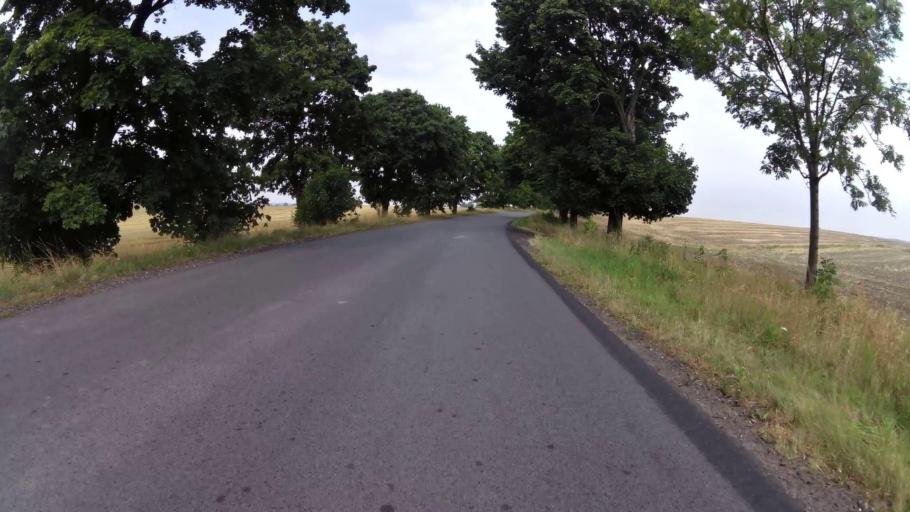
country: PL
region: West Pomeranian Voivodeship
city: Trzcinsko Zdroj
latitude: 52.9472
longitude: 14.6351
